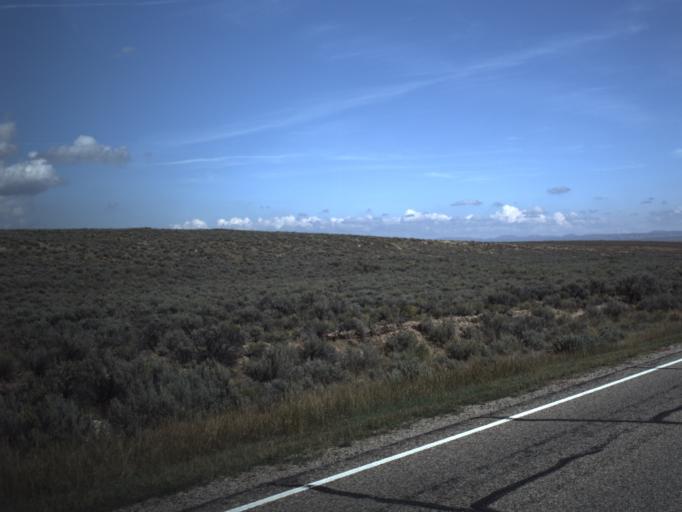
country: US
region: Utah
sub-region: Rich County
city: Randolph
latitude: 41.7712
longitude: -111.1364
